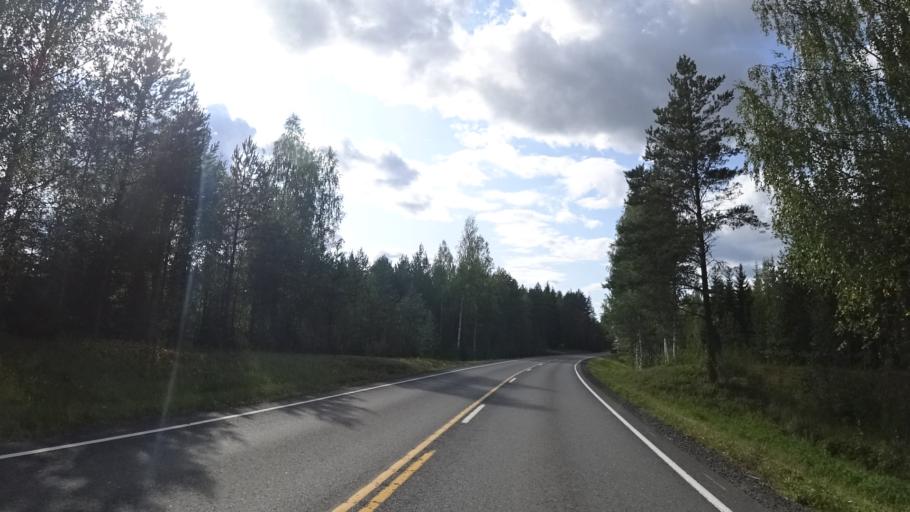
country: FI
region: North Karelia
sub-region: Keski-Karjala
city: Tohmajaervi
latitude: 62.1846
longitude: 30.5050
